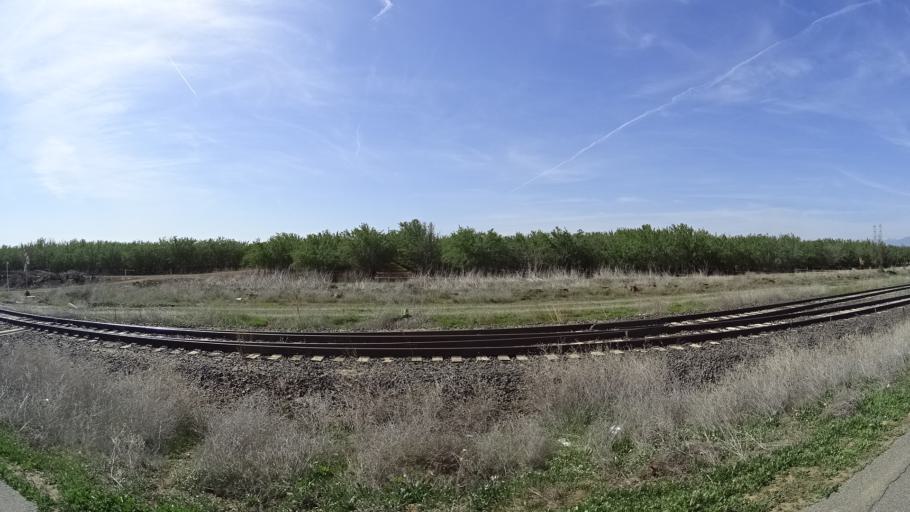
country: US
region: California
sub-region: Glenn County
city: Willows
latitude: 39.5318
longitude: -122.2591
